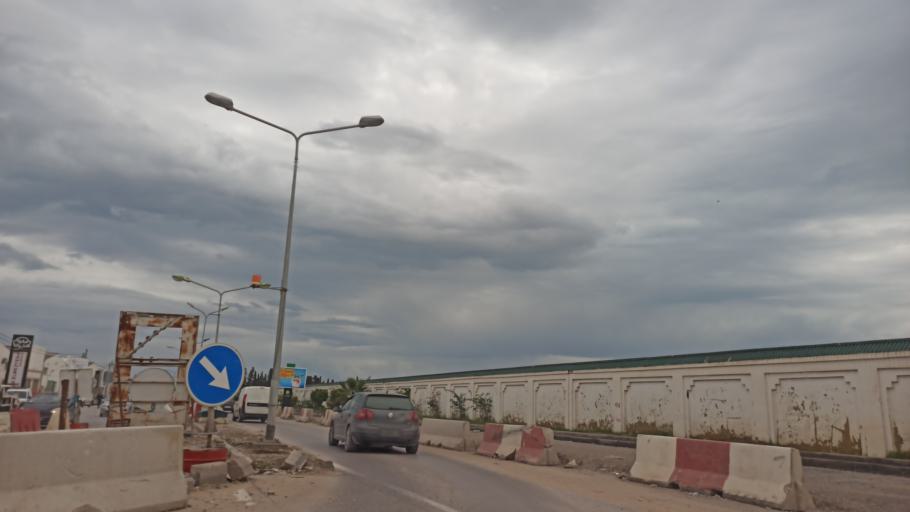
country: TN
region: Ariana
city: Ariana
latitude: 36.8698
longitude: 10.2306
